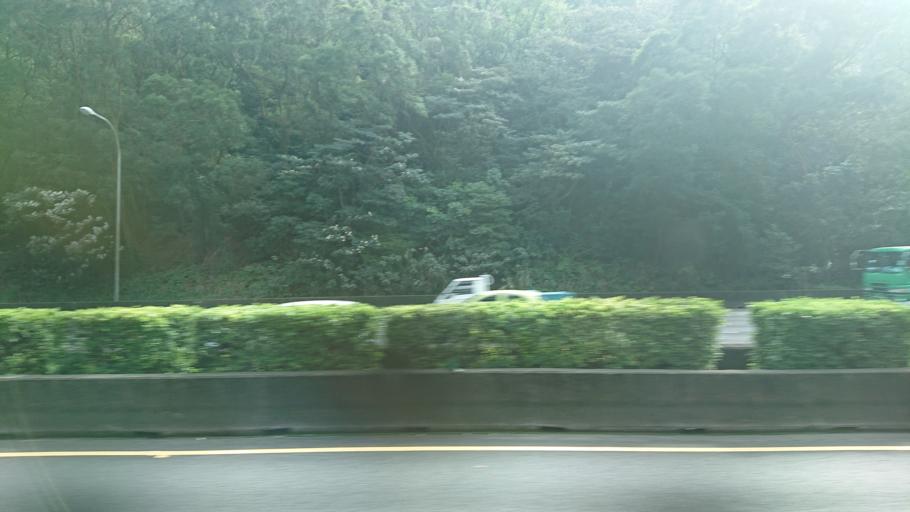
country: TW
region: Taipei
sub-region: Taipei
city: Banqiao
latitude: 25.0650
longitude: 121.3854
